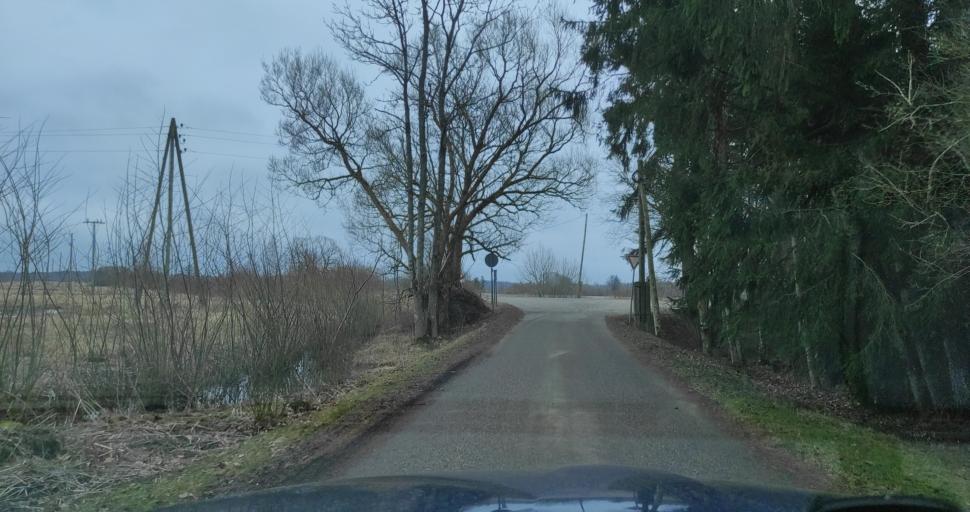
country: LV
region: Ventspils Rajons
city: Piltene
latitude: 57.2223
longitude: 21.6882
